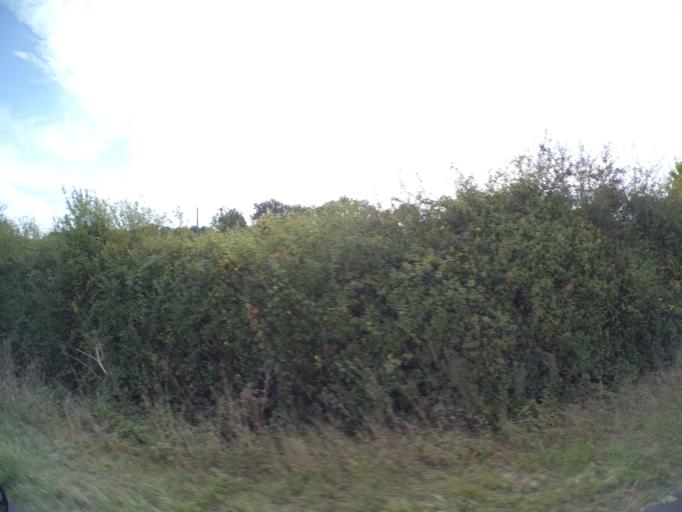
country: FR
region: Pays de la Loire
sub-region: Departement de Maine-et-Loire
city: Vihiers
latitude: 47.2073
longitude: -0.5509
